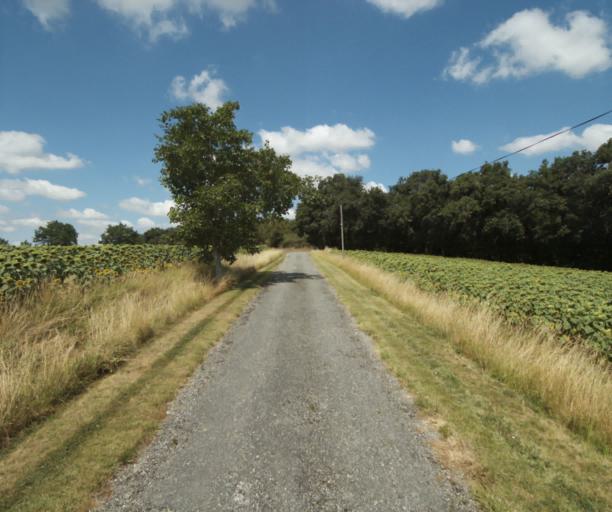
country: FR
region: Midi-Pyrenees
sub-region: Departement de la Haute-Garonne
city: Auriac-sur-Vendinelle
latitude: 43.4744
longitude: 1.7971
